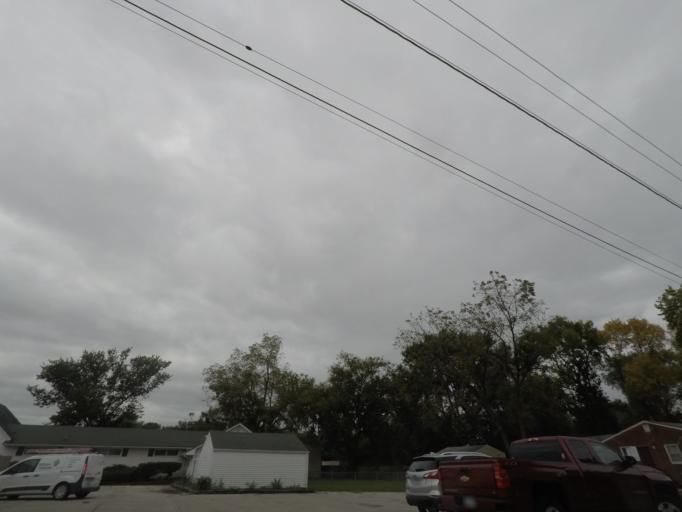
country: US
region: Iowa
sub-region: Warren County
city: Norwalk
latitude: 41.5269
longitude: -93.6354
